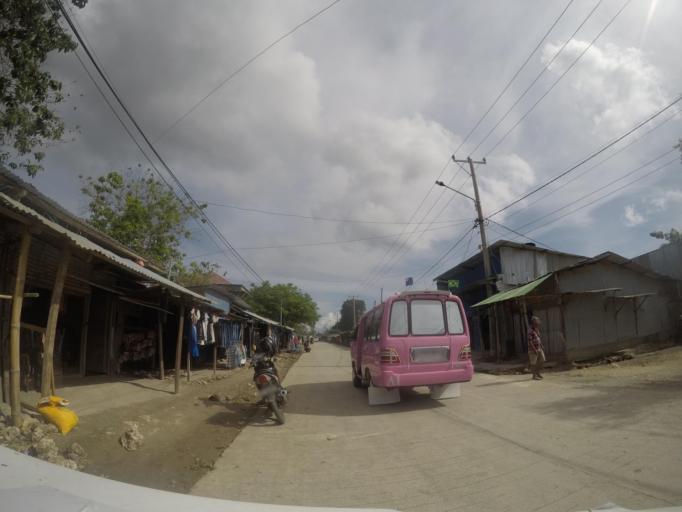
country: TL
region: Baucau
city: Baucau
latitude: -8.4814
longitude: 126.4524
